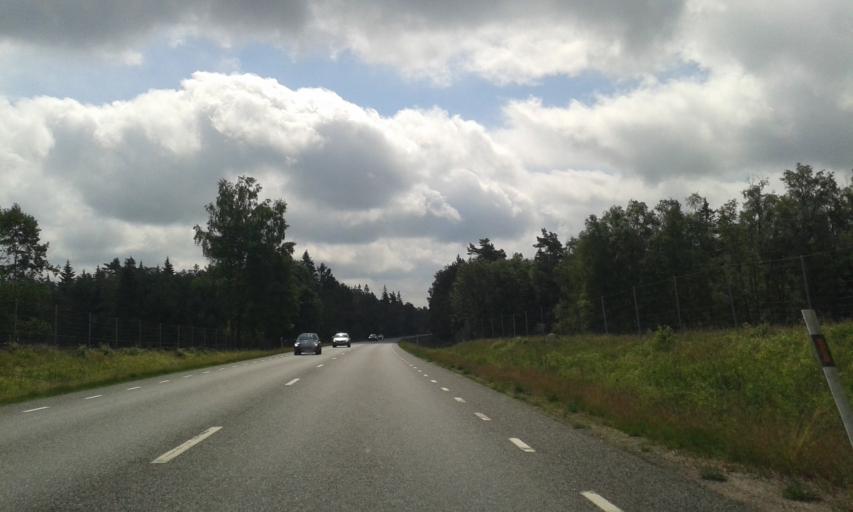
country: SE
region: Vaestra Goetaland
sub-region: Tranemo Kommun
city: Limmared
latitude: 57.5463
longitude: 13.3278
